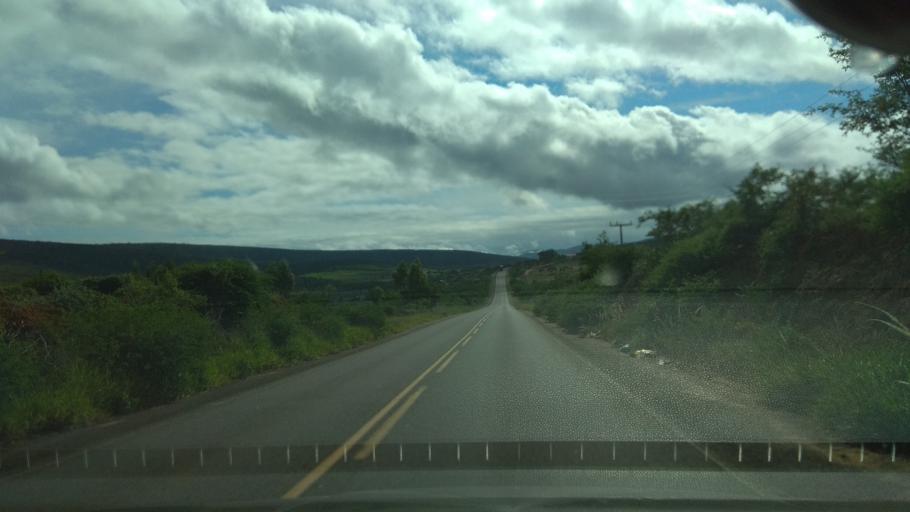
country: BR
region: Bahia
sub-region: Jaguaquara
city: Jaguaquara
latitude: -13.4383
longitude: -39.9314
